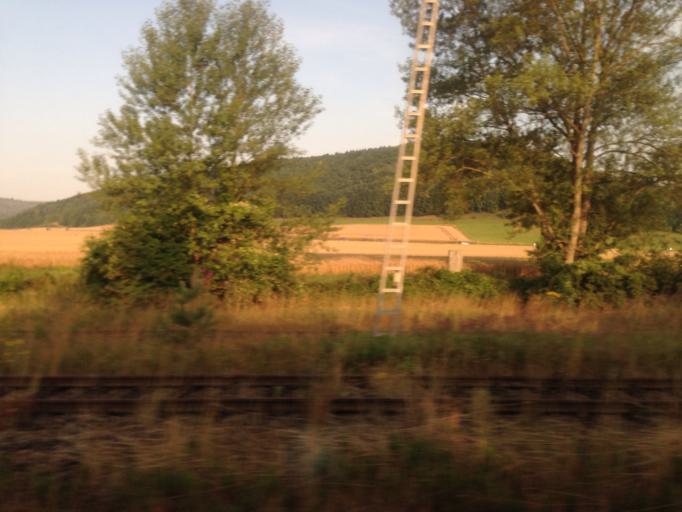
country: DE
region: Thuringia
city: Schops
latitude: 50.8314
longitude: 11.5969
